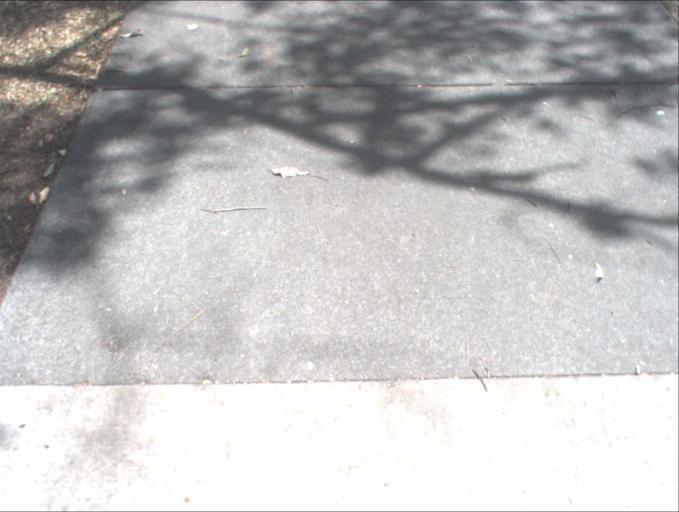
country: AU
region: Queensland
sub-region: Logan
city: Slacks Creek
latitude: -27.6453
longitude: 153.1732
